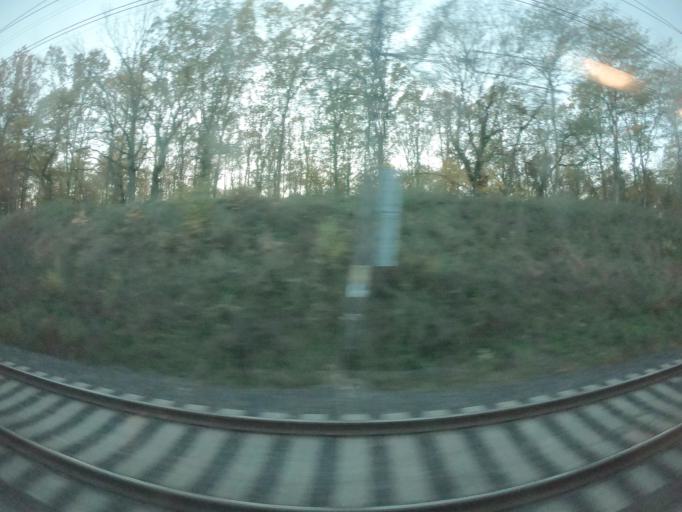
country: PL
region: West Pomeranian Voivodeship
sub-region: Powiat mysliborski
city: Boleszkowice
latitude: 52.7225
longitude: 14.5273
